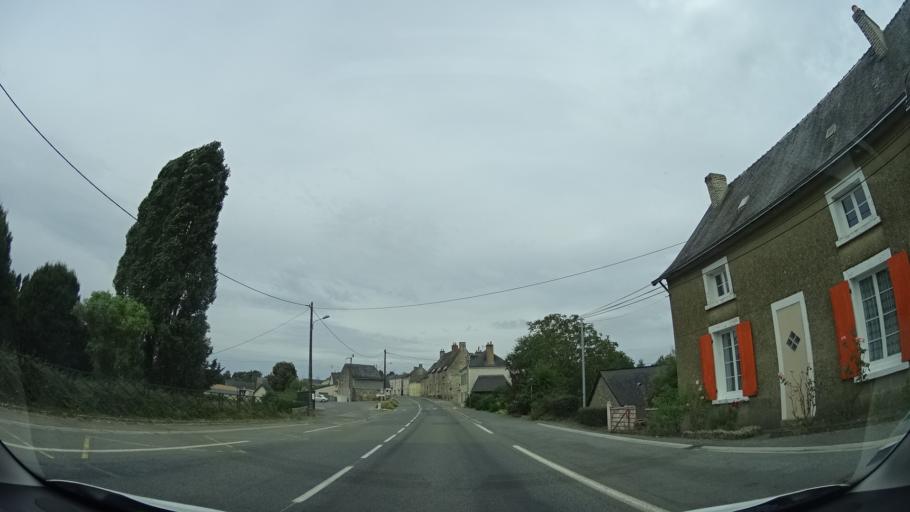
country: FR
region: Pays de la Loire
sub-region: Departement de la Sarthe
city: Auvers-le-Hamon
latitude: 47.8893
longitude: -0.4151
